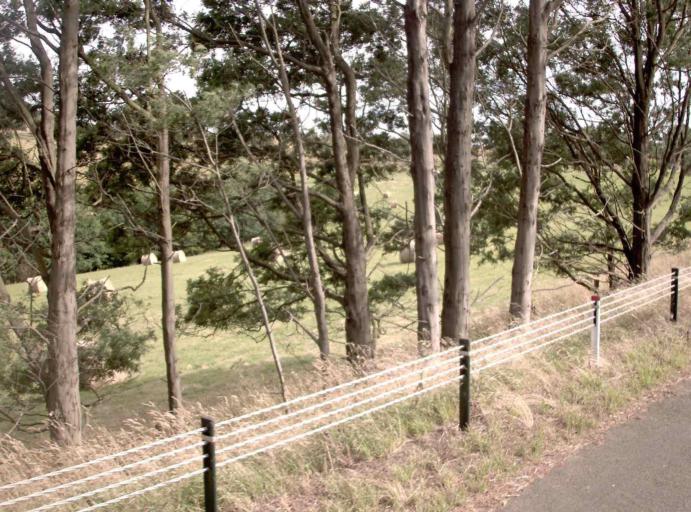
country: AU
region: Victoria
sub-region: Latrobe
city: Moe
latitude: -38.3357
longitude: 146.2010
